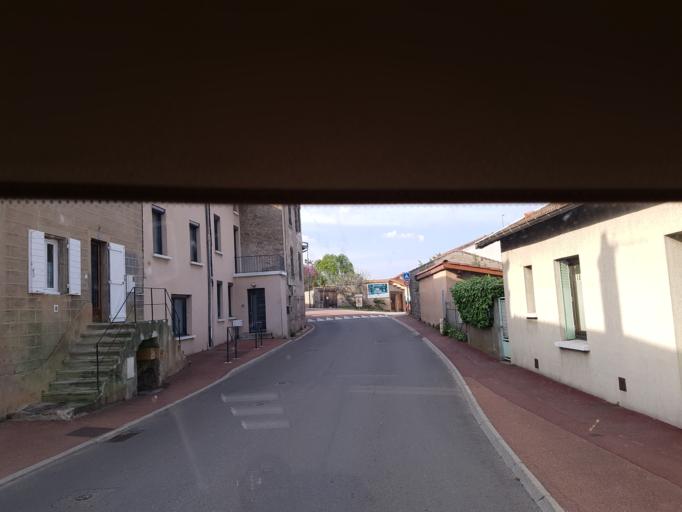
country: FR
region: Rhone-Alpes
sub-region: Departement du Rhone
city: Soucieu-en-Jarrest
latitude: 45.6792
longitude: 4.7039
